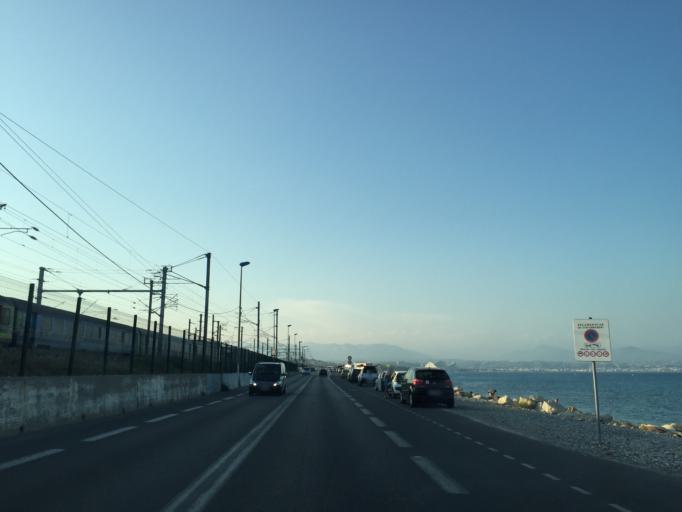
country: FR
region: Provence-Alpes-Cote d'Azur
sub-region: Departement des Alpes-Maritimes
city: Antibes
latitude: 43.5978
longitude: 7.1254
